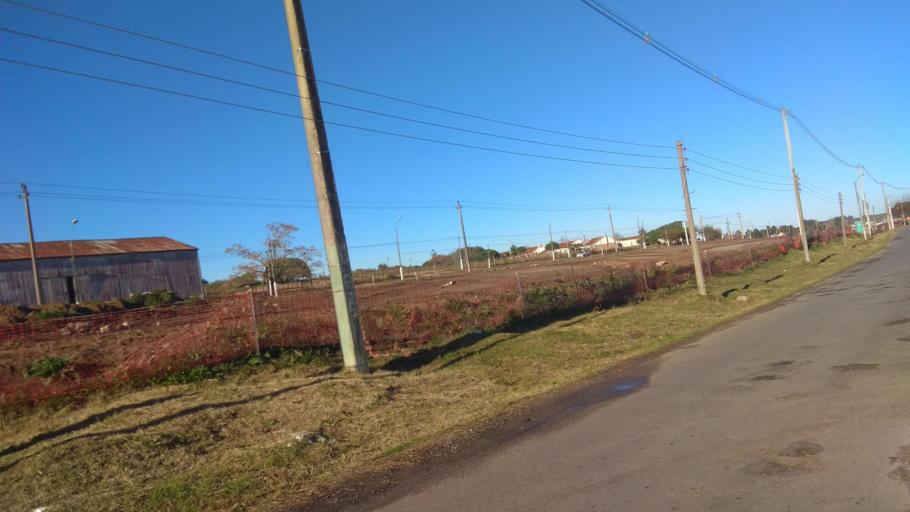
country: UY
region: Florida
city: Florida
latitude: -34.0995
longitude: -56.2365
